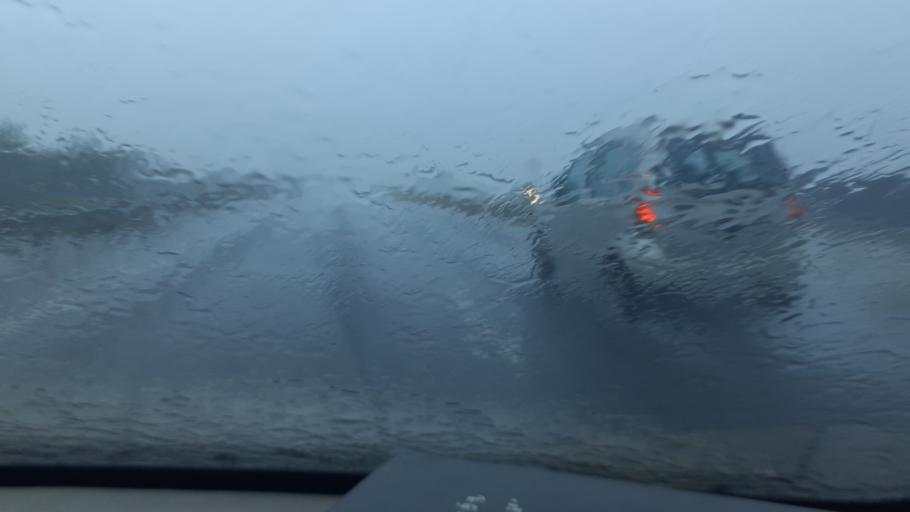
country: IN
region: Tamil Nadu
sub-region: Virudhunagar
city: Sattur
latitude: 9.4541
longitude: 77.9301
